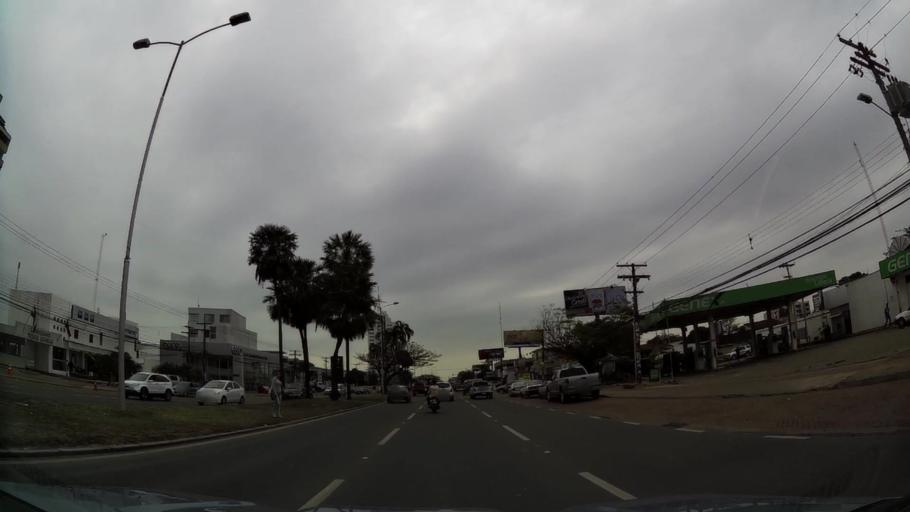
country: BO
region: Santa Cruz
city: Santa Cruz de la Sierra
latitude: -17.7648
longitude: -63.1810
